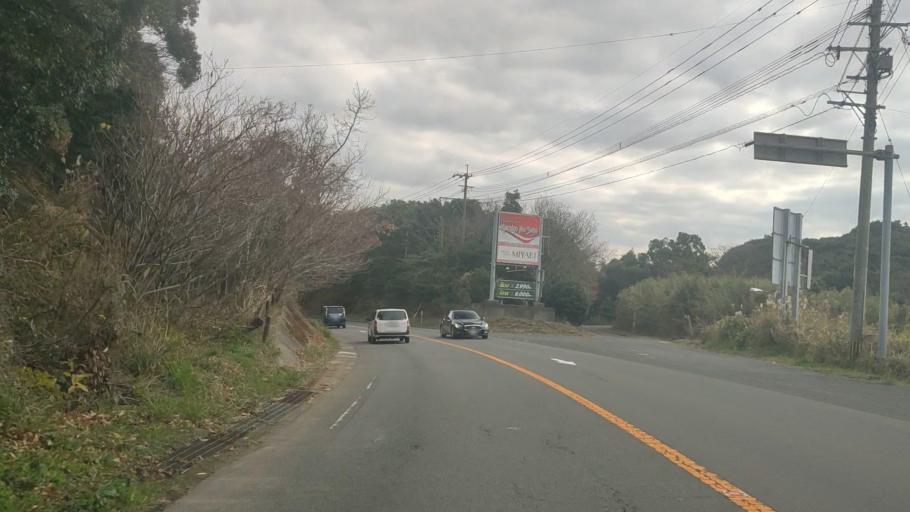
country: JP
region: Nagasaki
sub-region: Isahaya-shi
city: Isahaya
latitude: 32.7941
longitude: 130.1201
